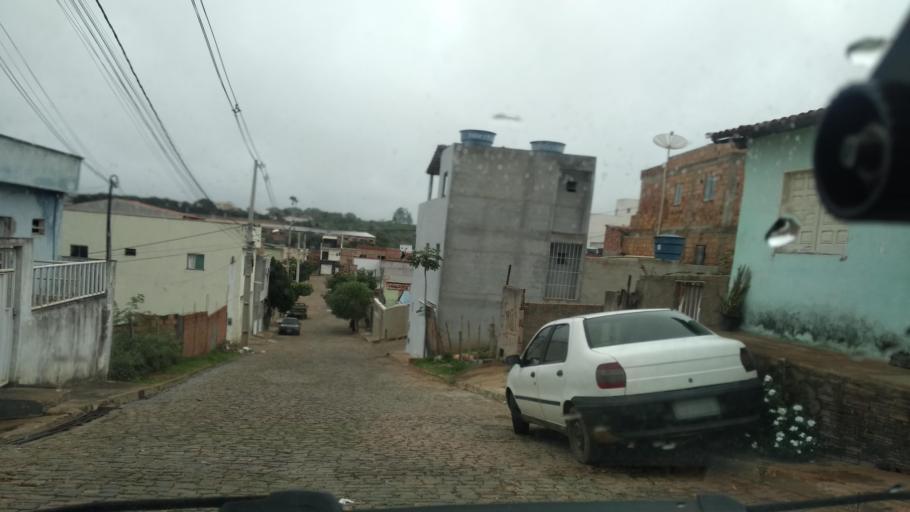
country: BR
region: Bahia
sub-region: Caetite
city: Caetite
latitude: -14.0630
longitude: -42.4814
